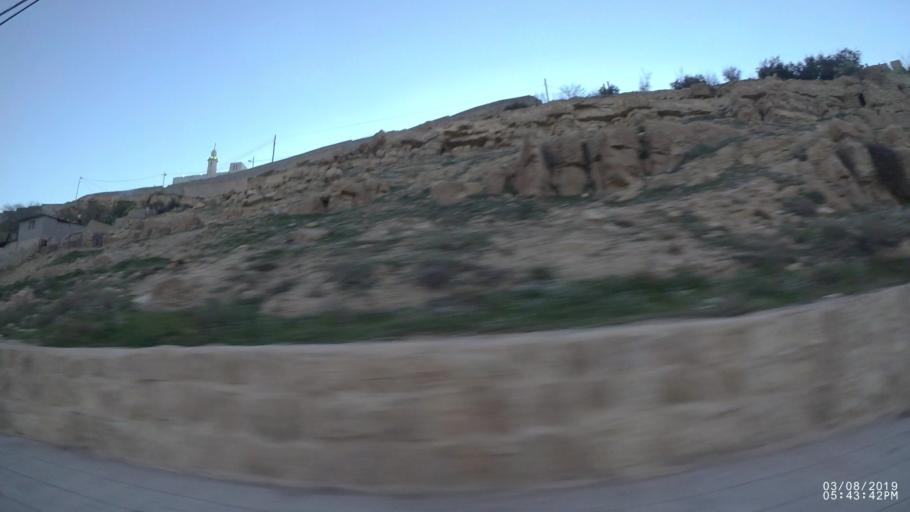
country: JO
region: Ma'an
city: Petra
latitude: 30.3130
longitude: 35.4786
